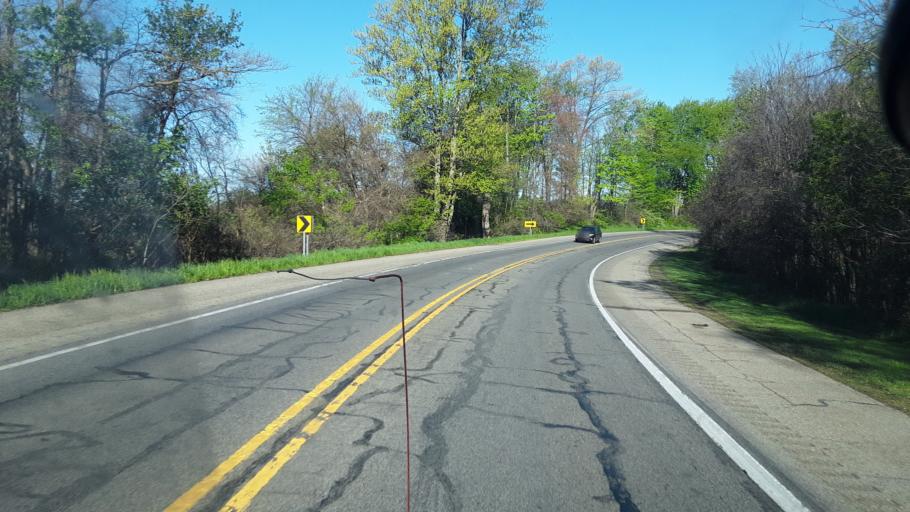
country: US
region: Indiana
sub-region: Steuben County
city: Angola
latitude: 41.6345
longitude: -85.1510
